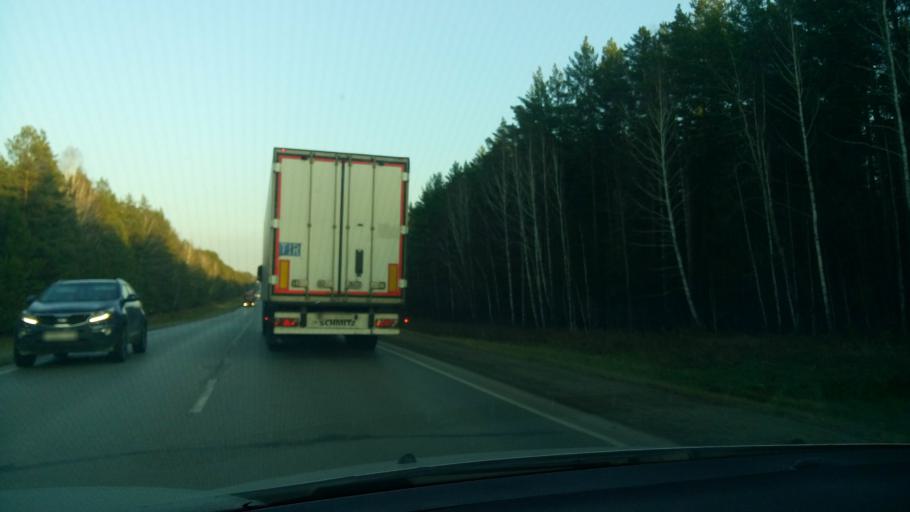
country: RU
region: Sverdlovsk
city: Yelanskiy
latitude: 56.7576
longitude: 62.2983
